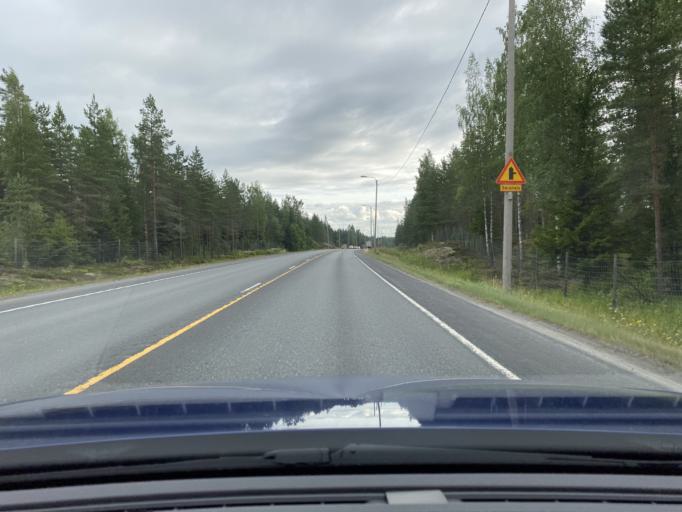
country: FI
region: Pirkanmaa
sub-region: Tampere
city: Kangasala
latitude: 61.5628
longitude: 24.0994
